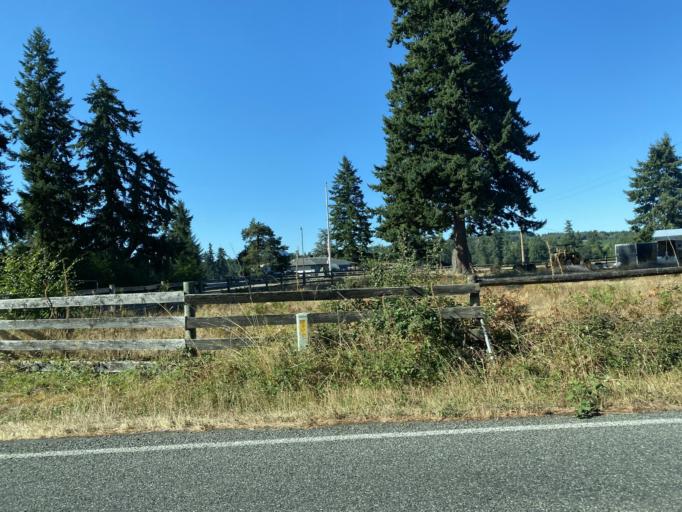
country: US
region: Washington
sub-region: Thurston County
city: Rainier
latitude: 46.8870
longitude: -122.7461
